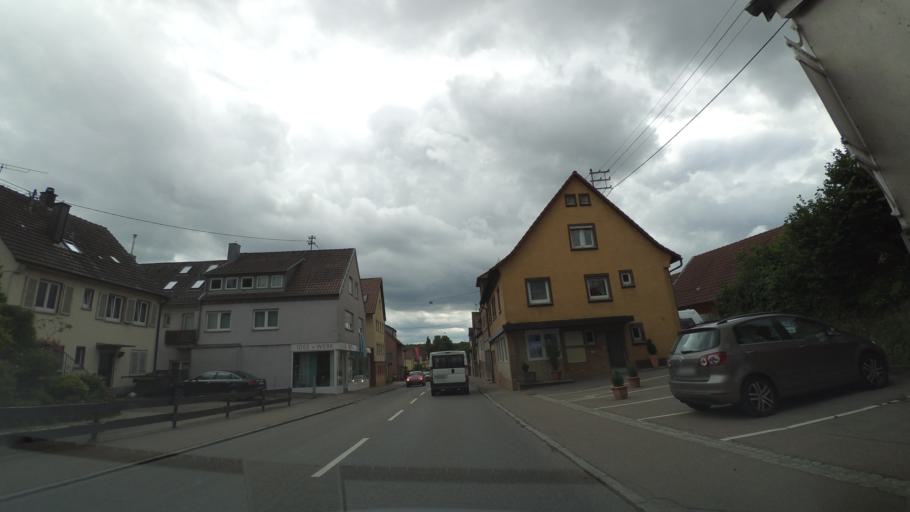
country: DE
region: Baden-Wuerttemberg
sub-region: Regierungsbezirk Stuttgart
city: Oppenweiler
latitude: 48.9824
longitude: 9.4581
